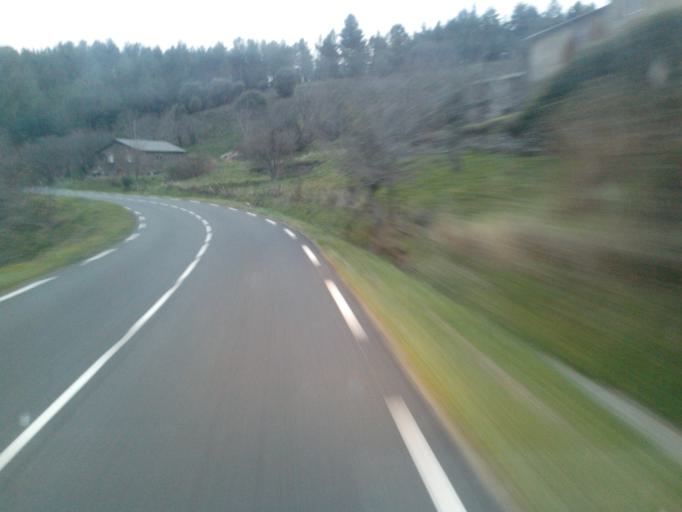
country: FR
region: Languedoc-Roussillon
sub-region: Departement du Gard
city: Valleraugue
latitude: 44.1623
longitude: 3.7293
